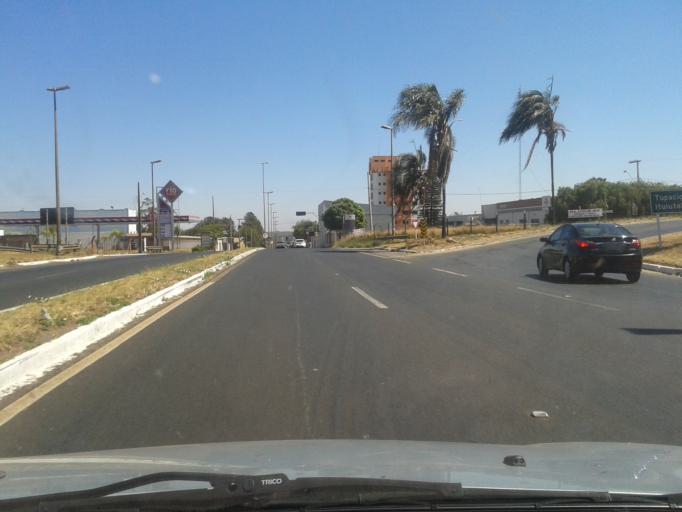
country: BR
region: Minas Gerais
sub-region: Uberlandia
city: Uberlandia
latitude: -18.8841
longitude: -48.2662
